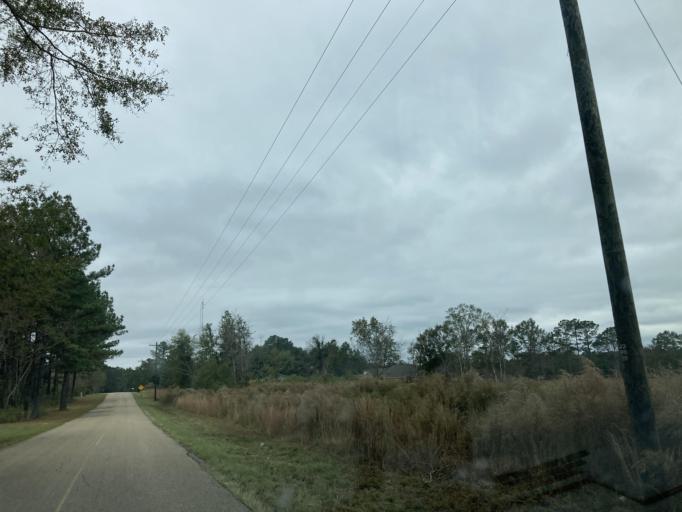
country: US
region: Mississippi
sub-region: Lamar County
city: West Hattiesburg
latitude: 31.2640
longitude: -89.5058
